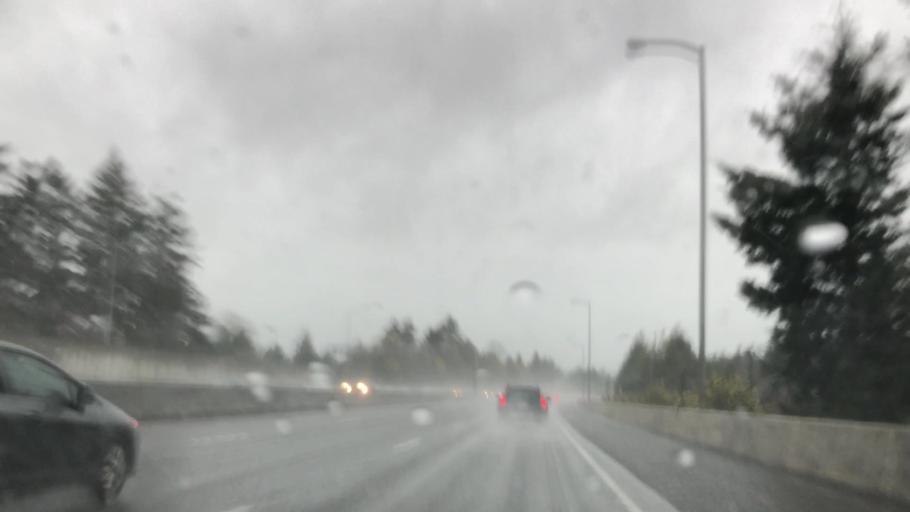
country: US
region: Oregon
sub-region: Washington County
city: West Slope
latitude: 45.5059
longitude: -122.7573
